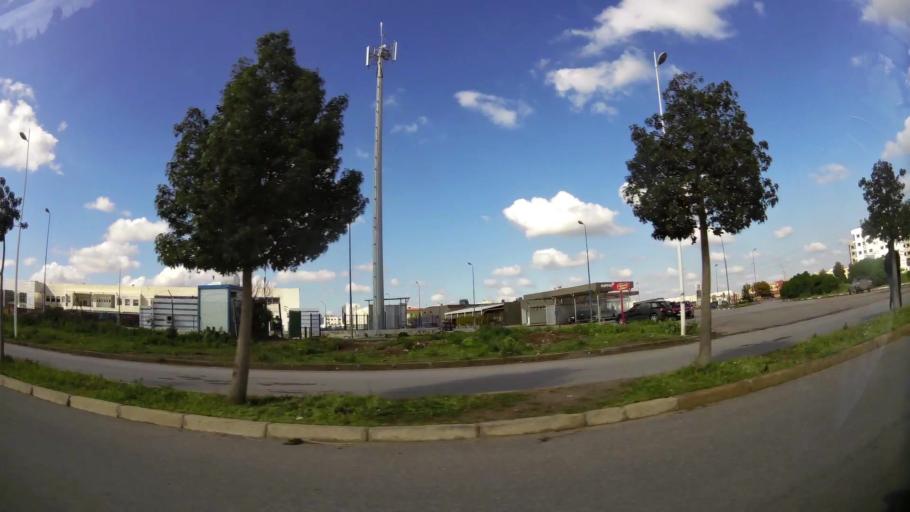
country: MA
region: Grand Casablanca
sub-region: Mediouna
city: Mediouna
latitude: 33.3882
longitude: -7.5377
